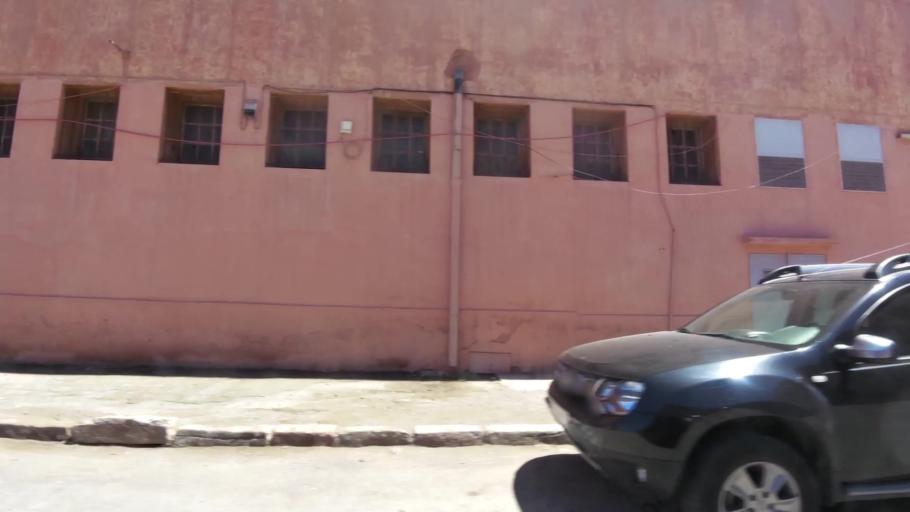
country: MA
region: Marrakech-Tensift-Al Haouz
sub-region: Marrakech
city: Marrakesh
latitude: 31.6284
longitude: -8.0174
